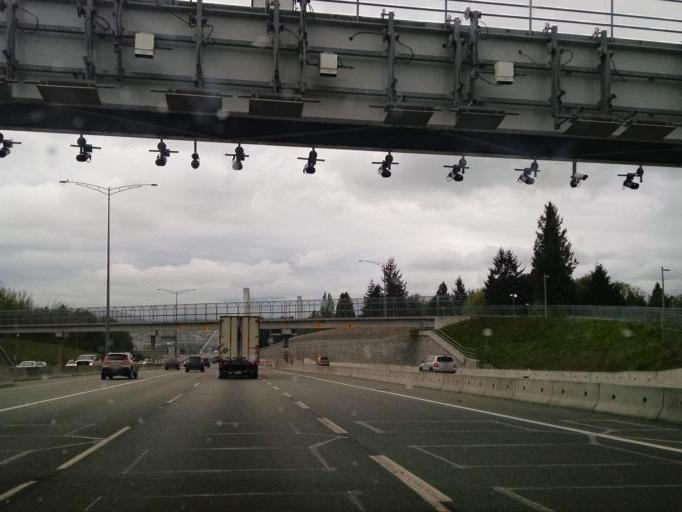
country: CA
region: British Columbia
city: Coquitlam
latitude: 49.2052
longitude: -122.8015
